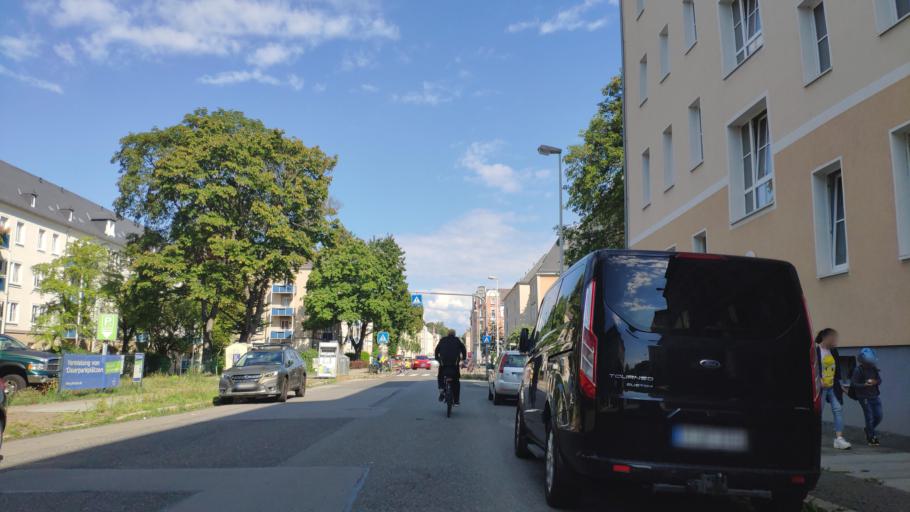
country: DE
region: Saxony
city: Chemnitz
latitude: 50.8281
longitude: 12.9362
